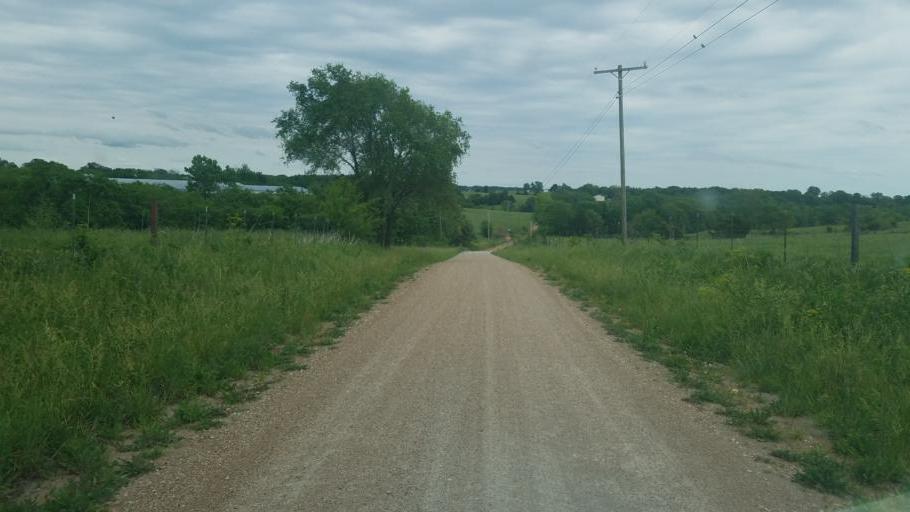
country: US
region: Missouri
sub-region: Moniteau County
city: California
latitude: 38.6217
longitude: -92.6208
